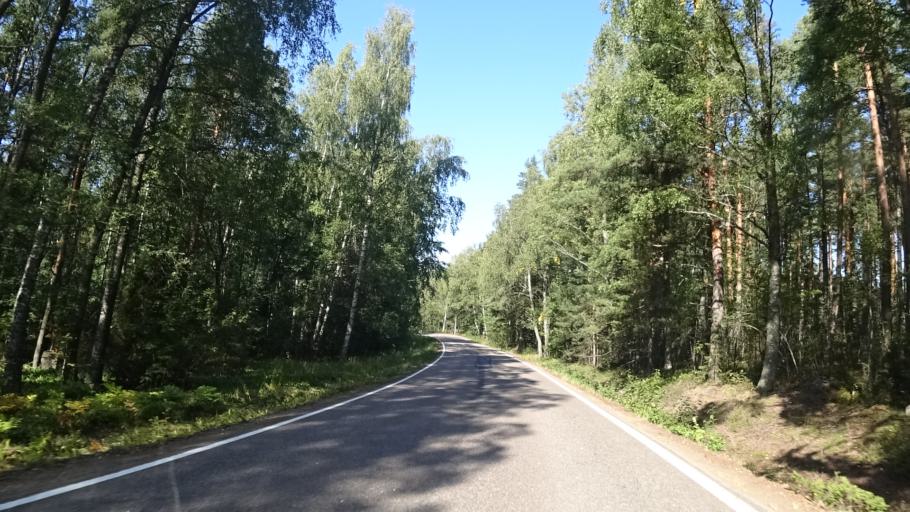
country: FI
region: Kymenlaakso
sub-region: Kotka-Hamina
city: Hamina
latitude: 60.5398
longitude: 27.2683
